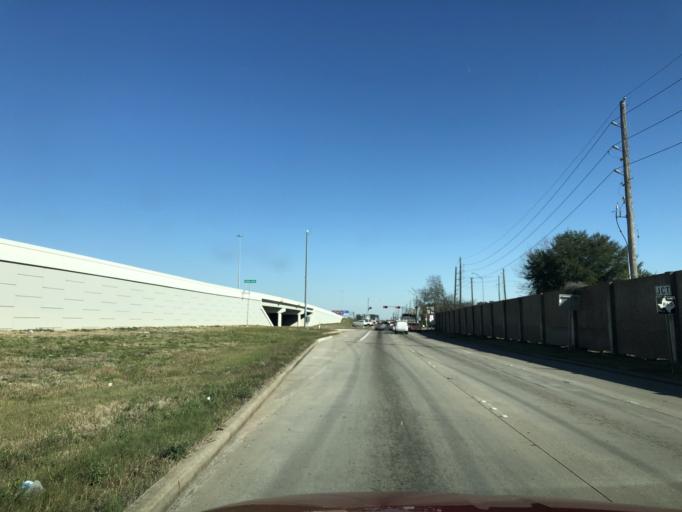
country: US
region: Texas
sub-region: Brazoria County
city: Brookside Village
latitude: 29.5981
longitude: -95.3550
